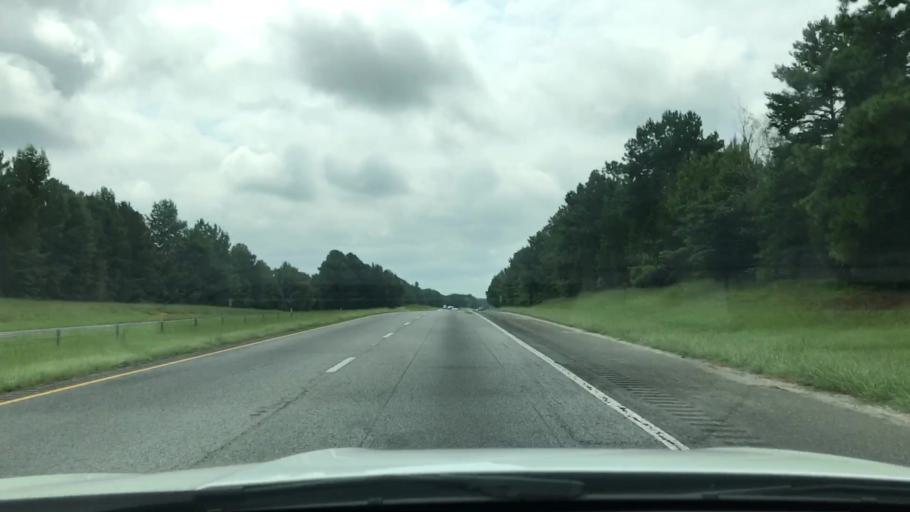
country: US
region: South Carolina
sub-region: Spartanburg County
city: Woodruff
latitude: 34.6590
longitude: -81.9243
